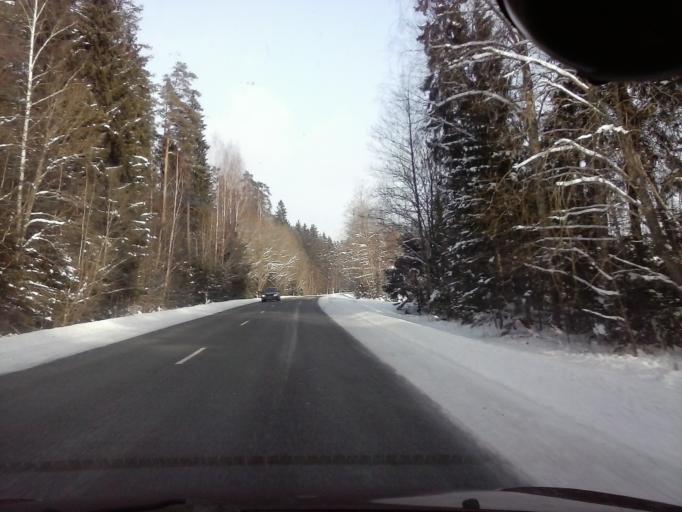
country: EE
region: Viljandimaa
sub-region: Moisakuela linn
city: Moisakula
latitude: 58.2551
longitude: 25.2020
